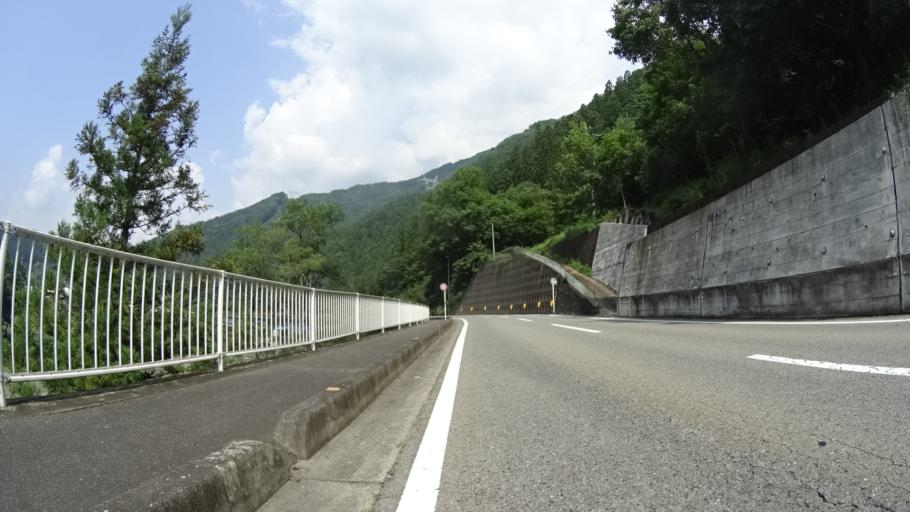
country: JP
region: Gunma
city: Tomioka
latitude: 36.0850
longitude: 138.7897
